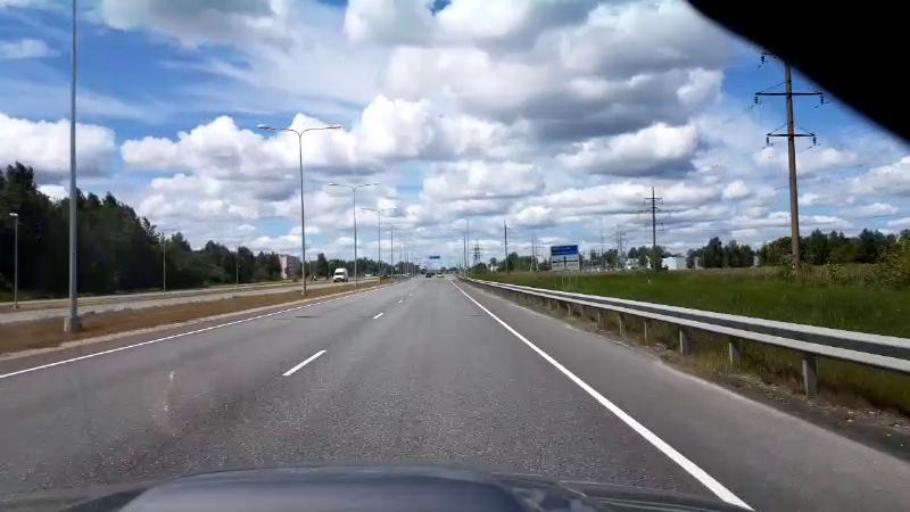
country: EE
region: Paernumaa
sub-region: Paernu linn
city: Parnu
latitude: 58.3920
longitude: 24.5401
